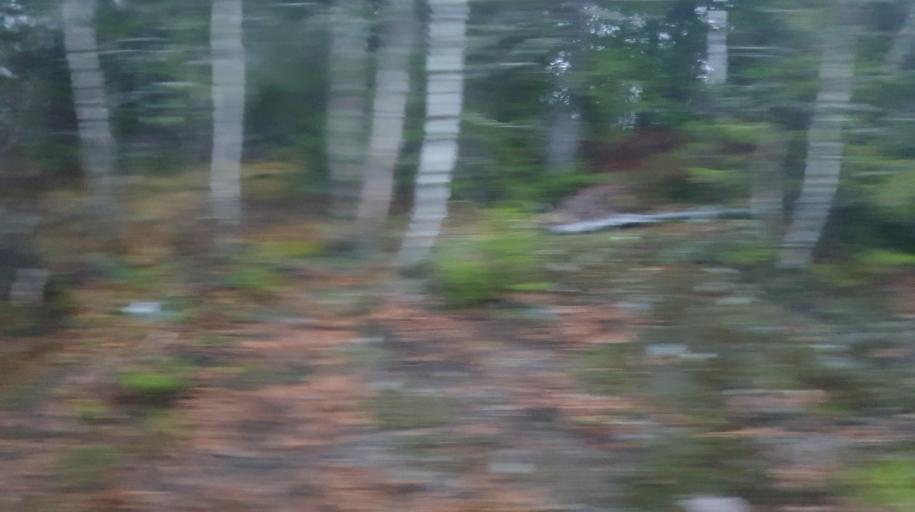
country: NO
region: Buskerud
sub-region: Krodsherad
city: Noresund
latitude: 60.2157
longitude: 9.5459
